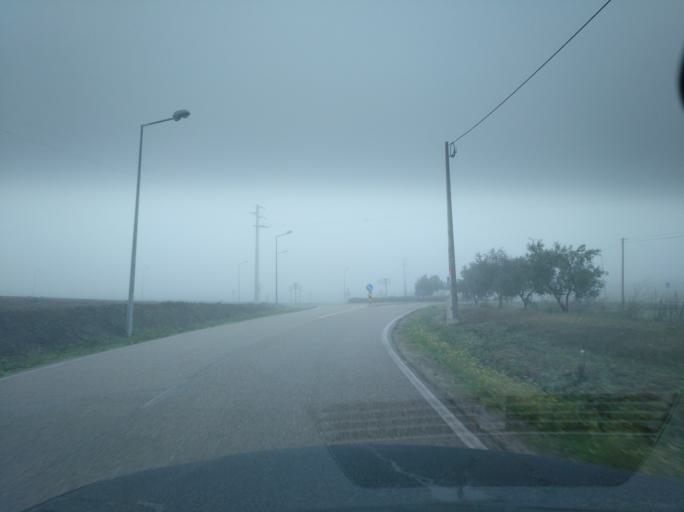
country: PT
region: Portalegre
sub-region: Campo Maior
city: Campo Maior
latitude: 39.0253
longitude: -7.0681
